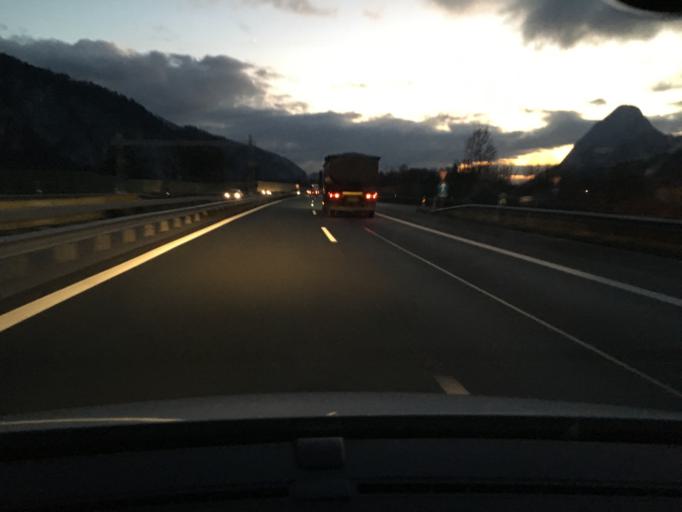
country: DE
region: Bavaria
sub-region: Upper Bavaria
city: Kiefersfelden
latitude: 47.6103
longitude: 12.2001
